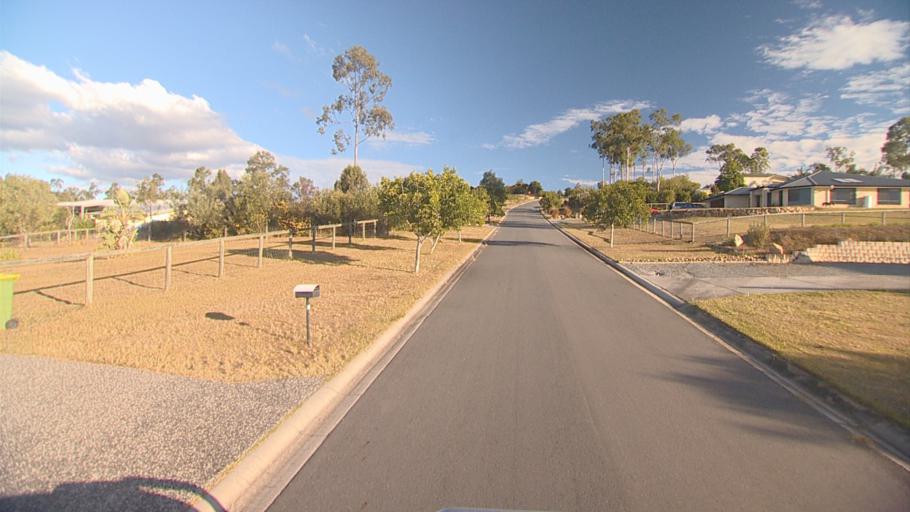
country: AU
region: Queensland
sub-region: Logan
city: Cedar Vale
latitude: -27.8640
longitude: 153.0840
